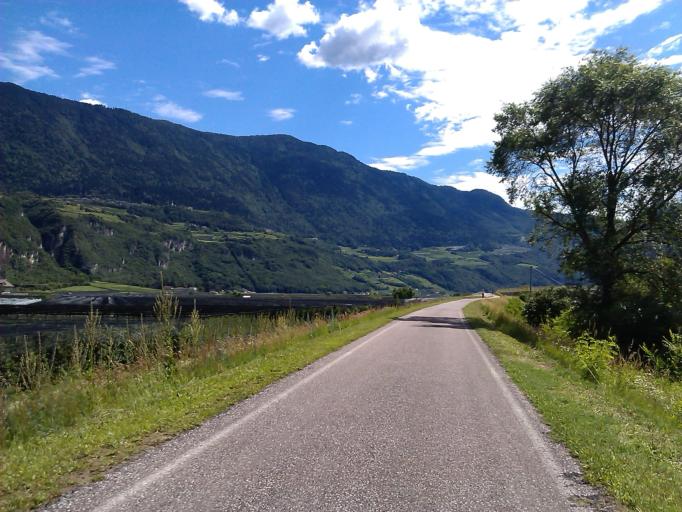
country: IT
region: Trentino-Alto Adige
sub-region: Bolzano
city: Laghetti
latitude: 46.2718
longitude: 11.2346
